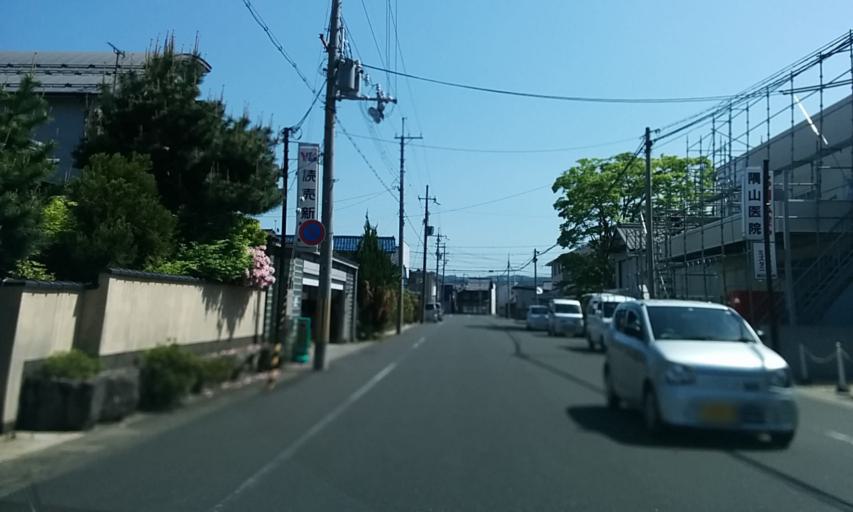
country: JP
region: Kyoto
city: Maizuru
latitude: 35.4524
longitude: 135.3248
